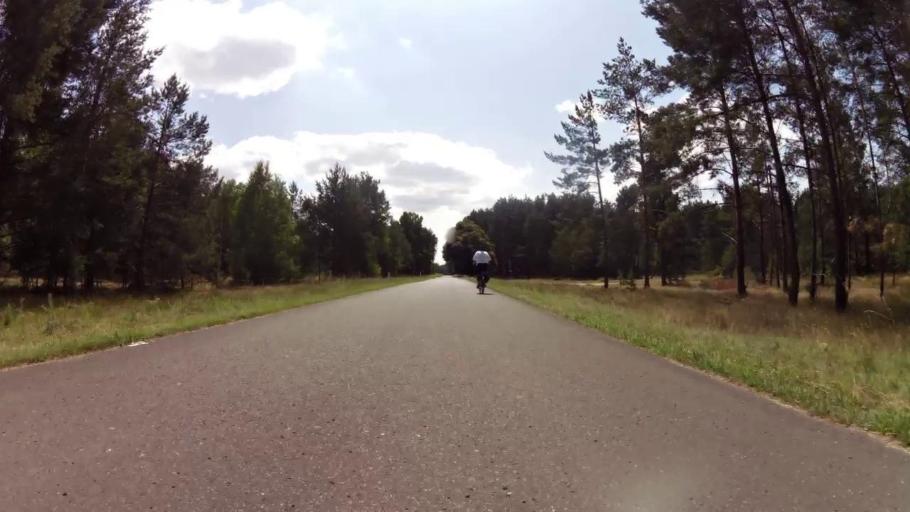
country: PL
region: West Pomeranian Voivodeship
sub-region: Powiat drawski
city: Drawsko Pomorskie
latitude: 53.3873
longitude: 15.7288
